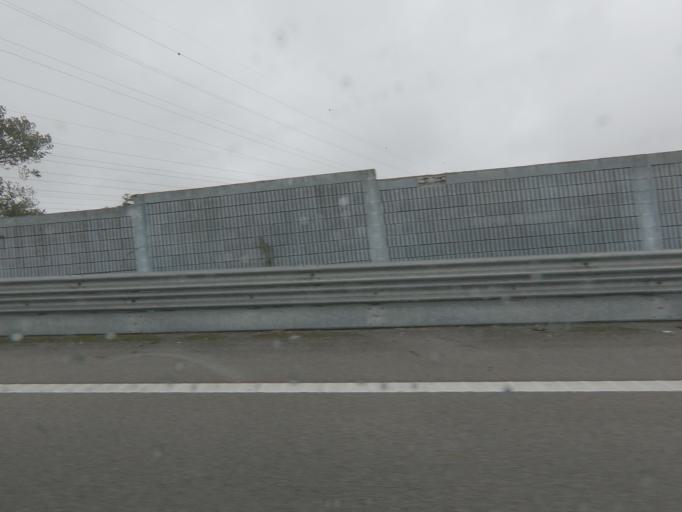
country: PT
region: Porto
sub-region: Matosinhos
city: Senhora da Hora
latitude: 41.2033
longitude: -8.6467
